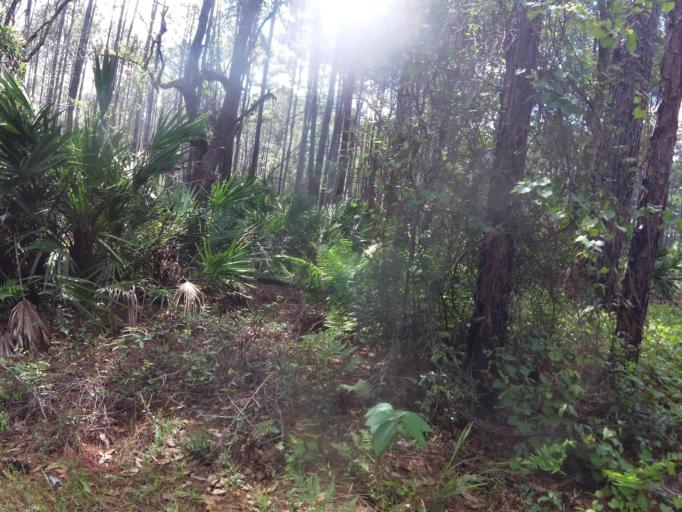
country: US
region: Florida
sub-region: Clay County
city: Green Cove Springs
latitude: 29.9716
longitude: -81.6410
